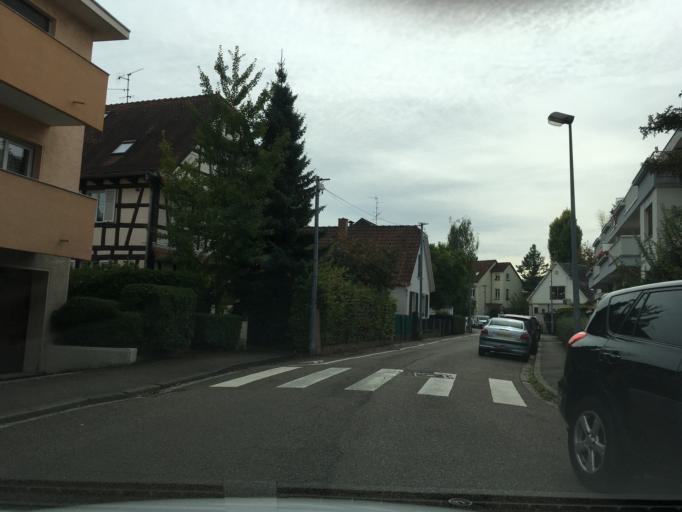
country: FR
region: Alsace
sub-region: Departement du Bas-Rhin
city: Bischheim
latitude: 48.6017
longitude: 7.7786
